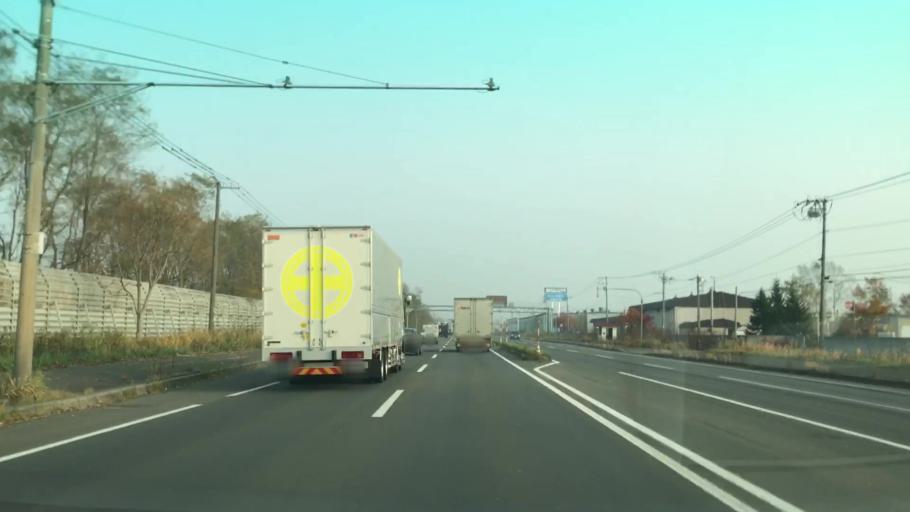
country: JP
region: Hokkaido
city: Ishikari
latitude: 43.1891
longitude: 141.3255
